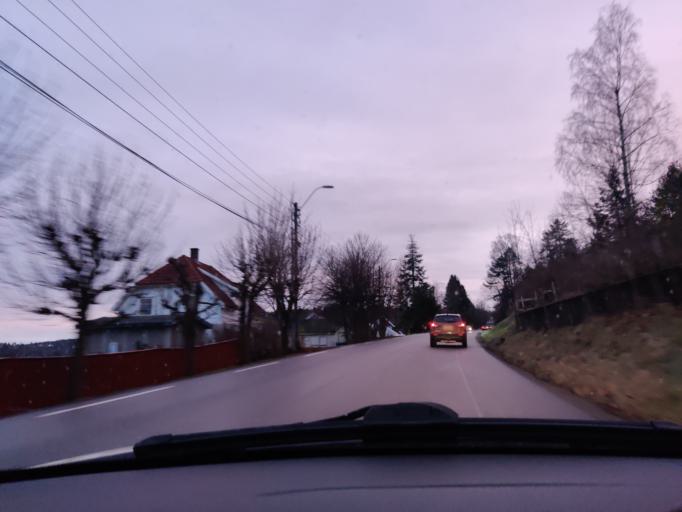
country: NO
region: Vestfold
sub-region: Tonsberg
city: Sem
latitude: 59.2734
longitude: 10.3658
